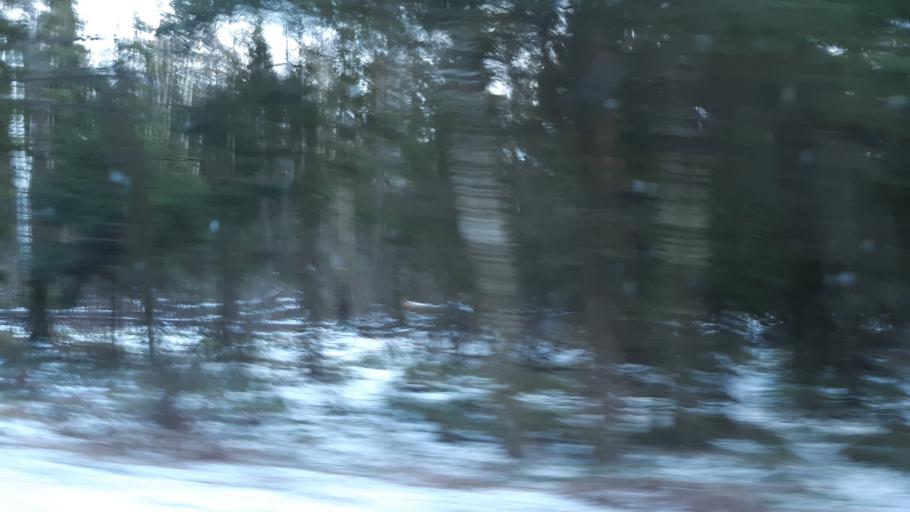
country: RU
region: Moskovskaya
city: Noginsk-9
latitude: 55.9756
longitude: 38.5406
